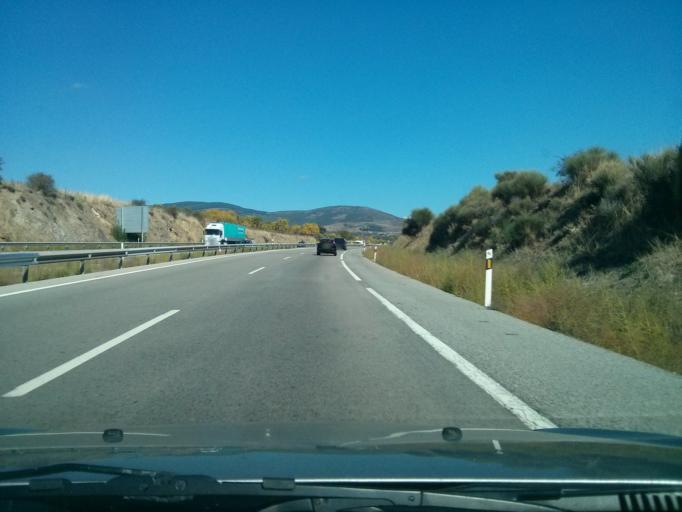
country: ES
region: Madrid
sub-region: Provincia de Madrid
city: Buitrago del Lozoya
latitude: 41.0048
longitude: -3.6373
